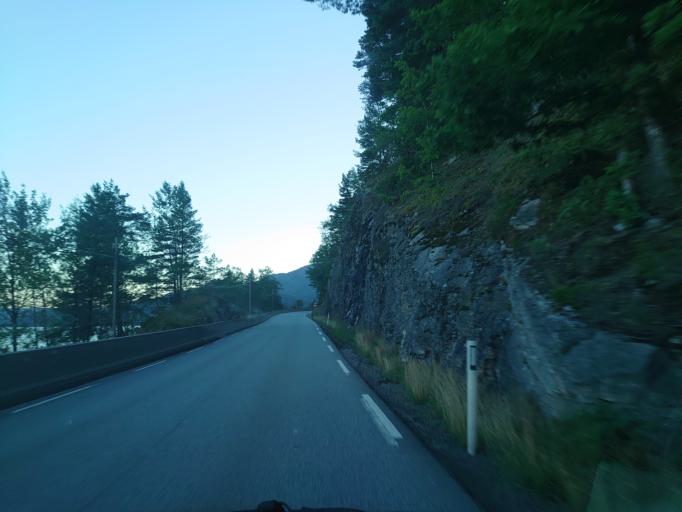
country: NO
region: Hordaland
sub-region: Modalen
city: Mo
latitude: 60.7105
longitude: 5.6155
